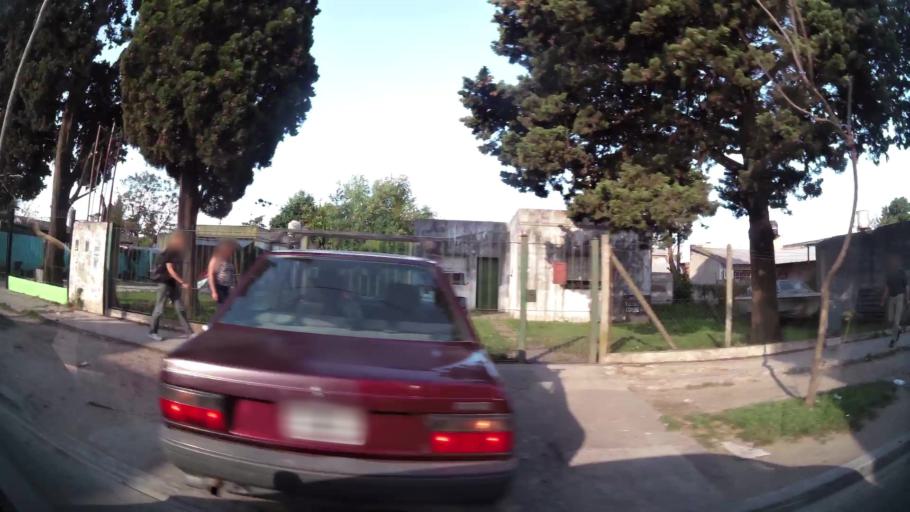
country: AR
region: Buenos Aires
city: Santa Catalina - Dique Lujan
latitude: -34.4919
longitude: -58.7222
